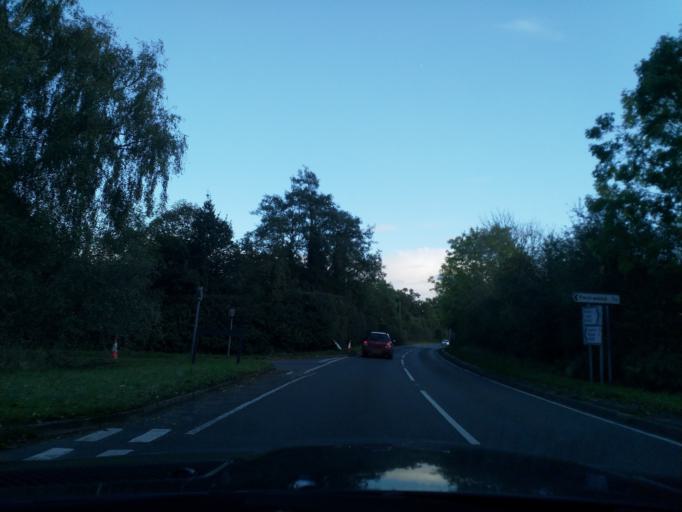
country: GB
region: England
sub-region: Solihull
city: Knowle
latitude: 52.3457
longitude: -1.7642
